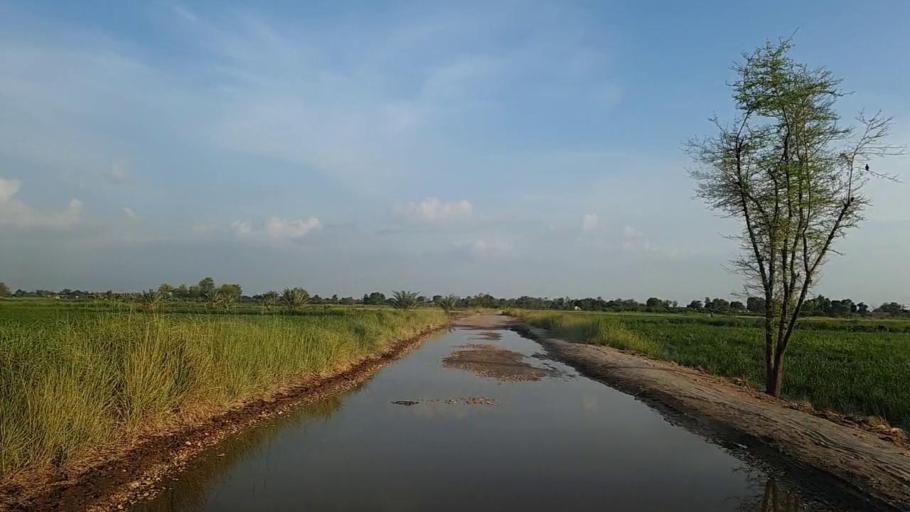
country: PK
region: Sindh
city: Karaundi
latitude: 27.0482
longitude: 68.4054
